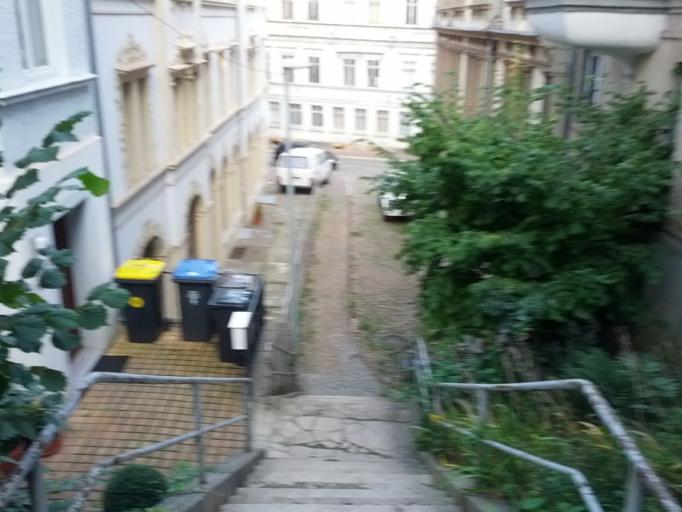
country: DE
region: Thuringia
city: Eisenach
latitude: 50.9691
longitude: 10.3220
